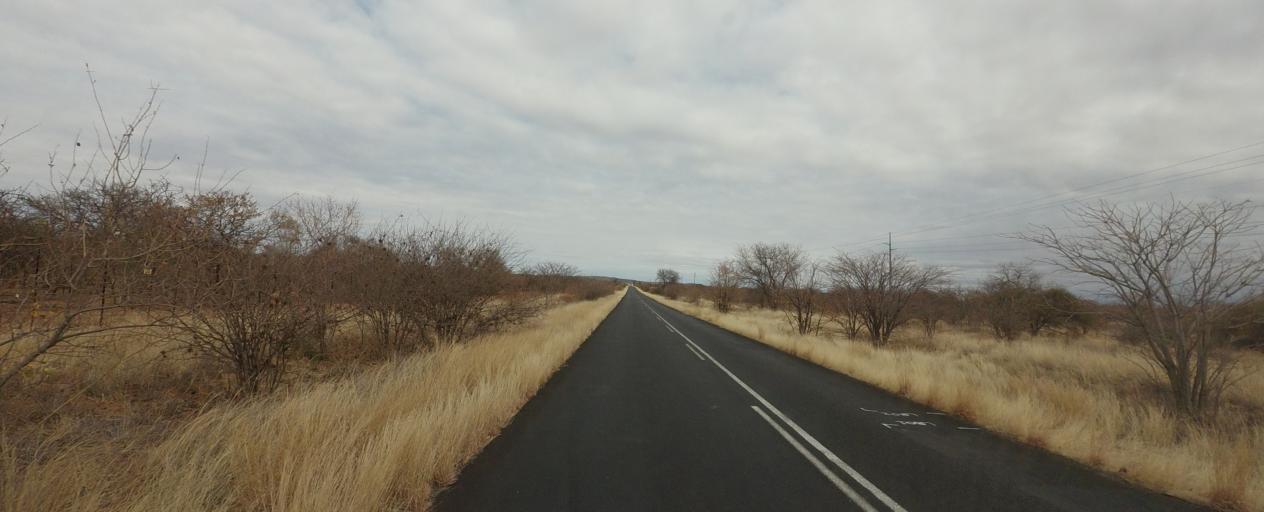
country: ZW
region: Matabeleland South
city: Beitbridge
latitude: -22.4315
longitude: 29.4662
